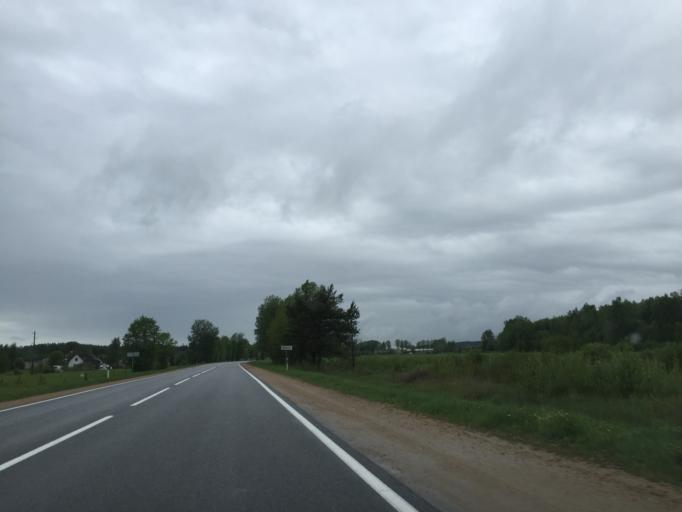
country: LV
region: Ogre
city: Ogre
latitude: 56.7747
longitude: 24.6606
